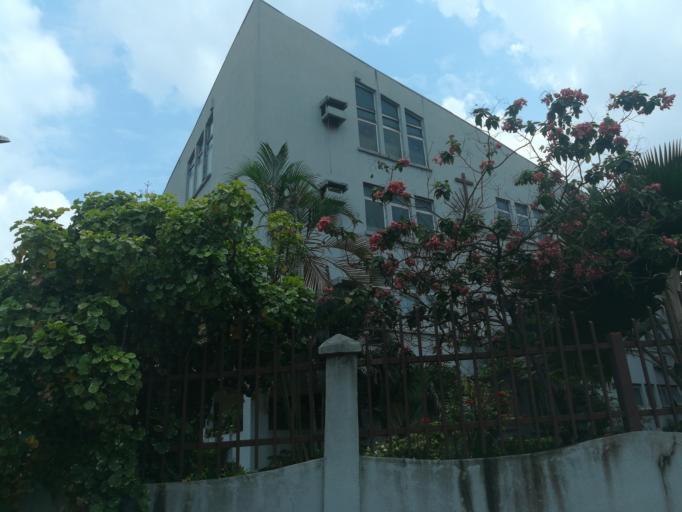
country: NG
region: Lagos
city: Ikeja
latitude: 6.5935
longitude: 3.3586
